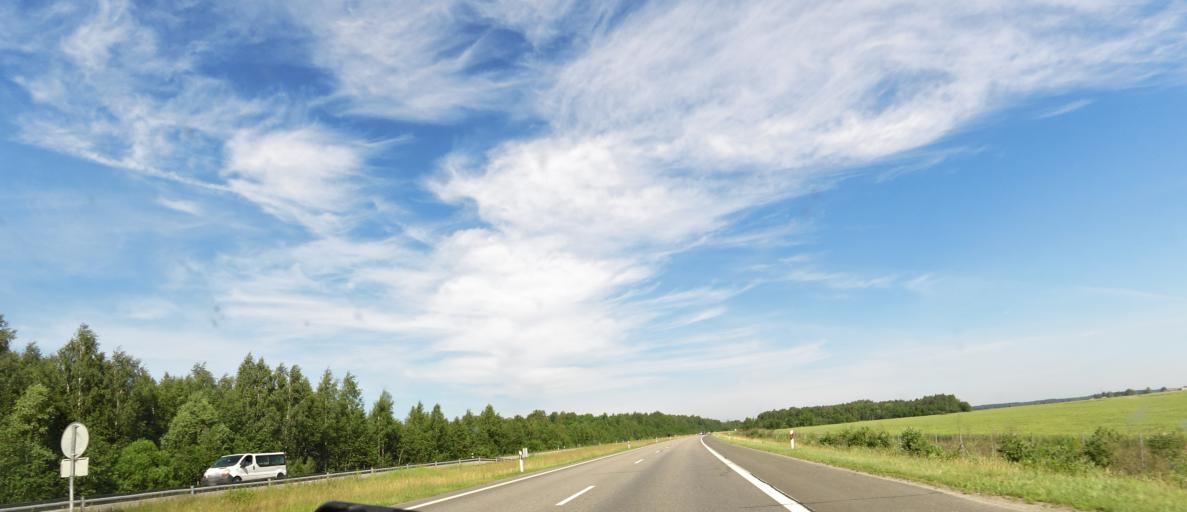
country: LT
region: Panevezys
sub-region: Panevezys City
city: Panevezys
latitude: 55.6182
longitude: 24.4141
